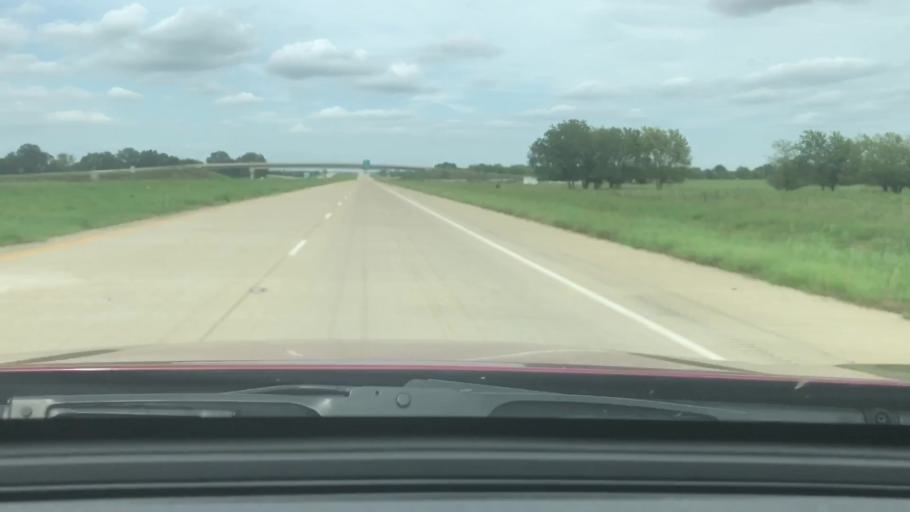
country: US
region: Louisiana
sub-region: Caddo Parish
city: Vivian
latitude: 32.8419
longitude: -93.8694
